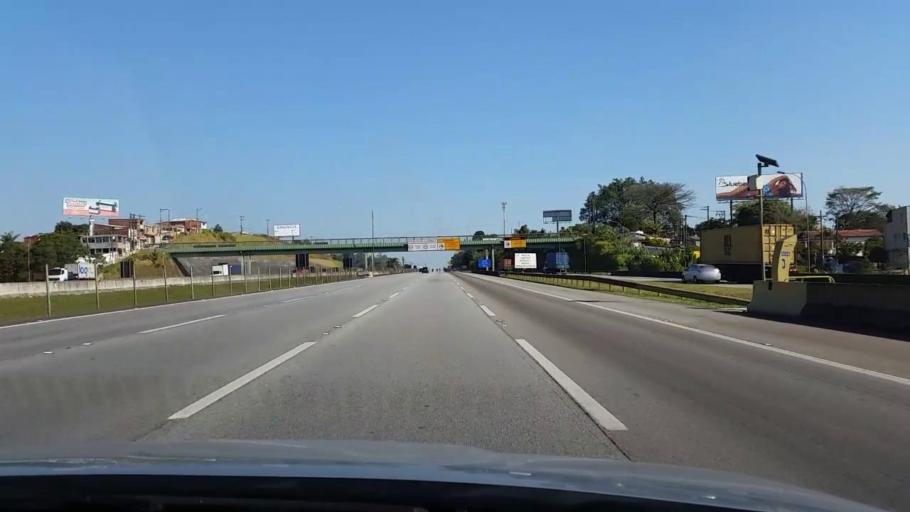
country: BR
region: Sao Paulo
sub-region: Sao Bernardo Do Campo
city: Sao Bernardo do Campo
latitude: -23.7697
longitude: -46.5925
